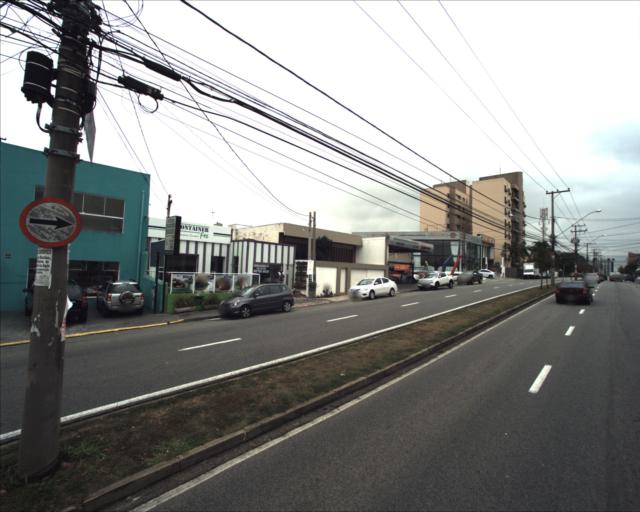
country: BR
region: Sao Paulo
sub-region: Sorocaba
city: Sorocaba
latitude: -23.5152
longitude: -47.4643
